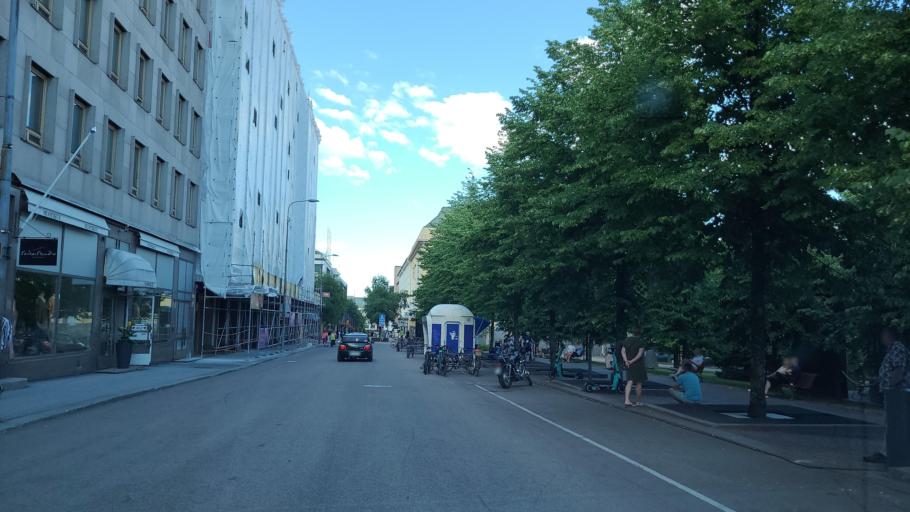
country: FI
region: Central Finland
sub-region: Jyvaeskylae
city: Jyvaeskylae
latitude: 62.2410
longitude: 25.7440
